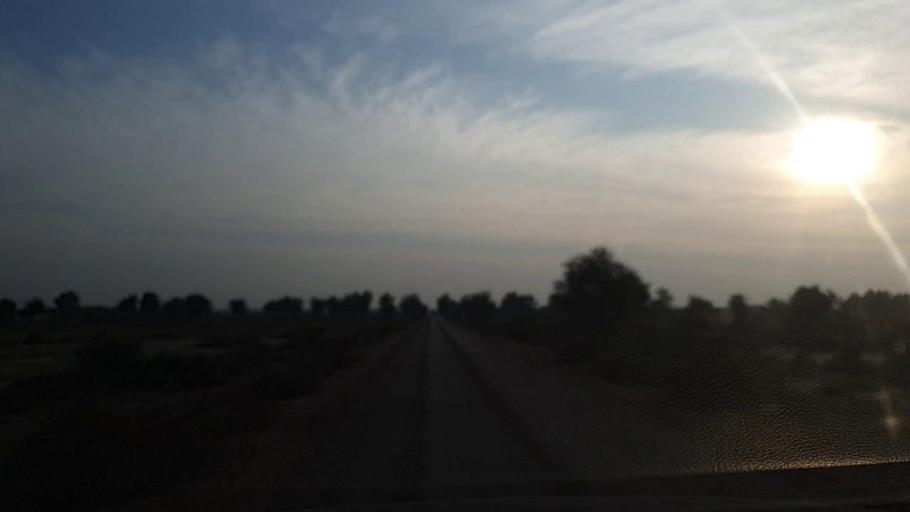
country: PK
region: Sindh
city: Jam Sahib
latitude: 26.4105
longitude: 68.5112
